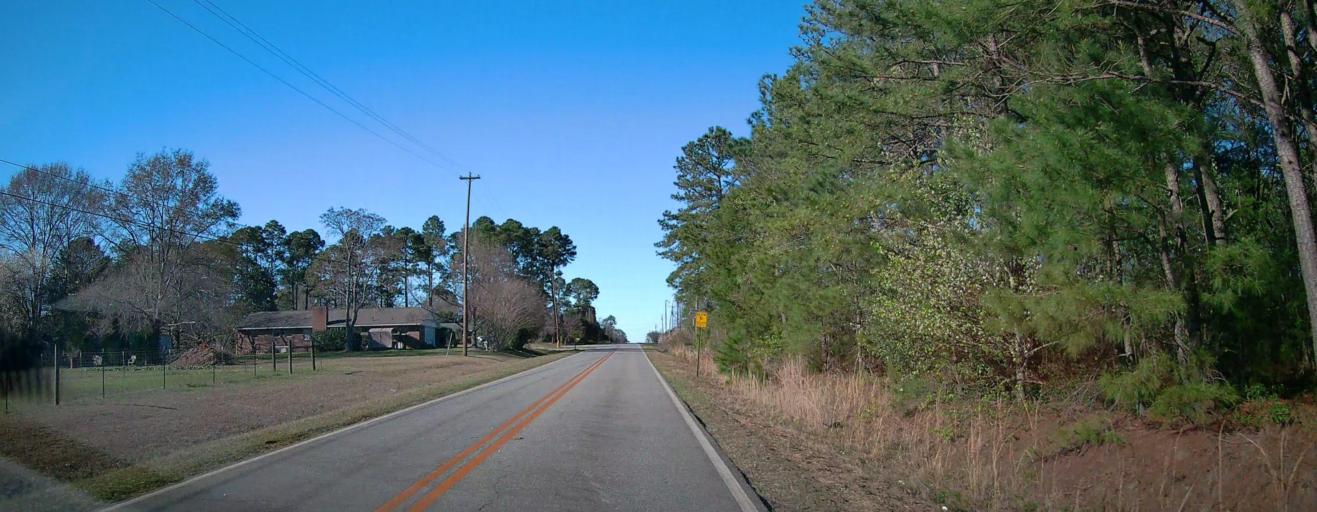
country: US
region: Georgia
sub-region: Peach County
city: Fort Valley
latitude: 32.5604
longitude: -83.9159
